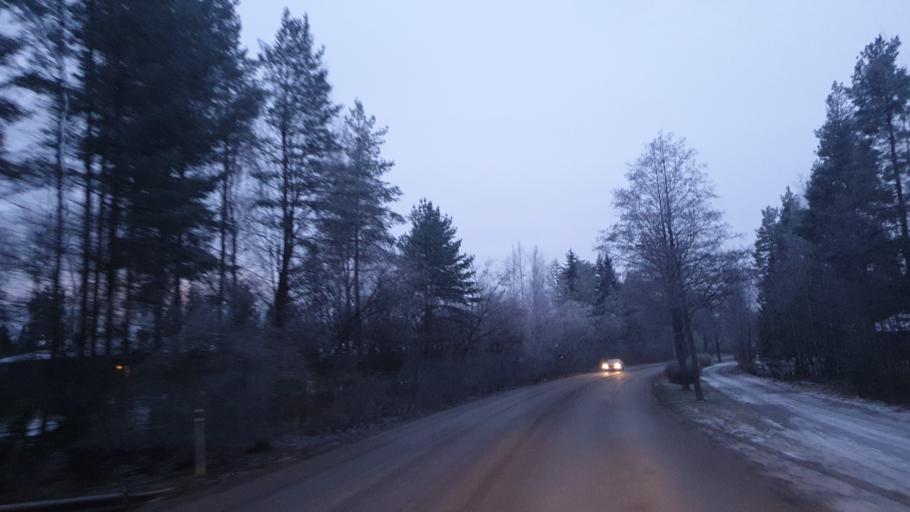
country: FI
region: Southern Ostrobothnia
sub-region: Seinaejoki
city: Seinaejoki
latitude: 62.7730
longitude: 22.8834
